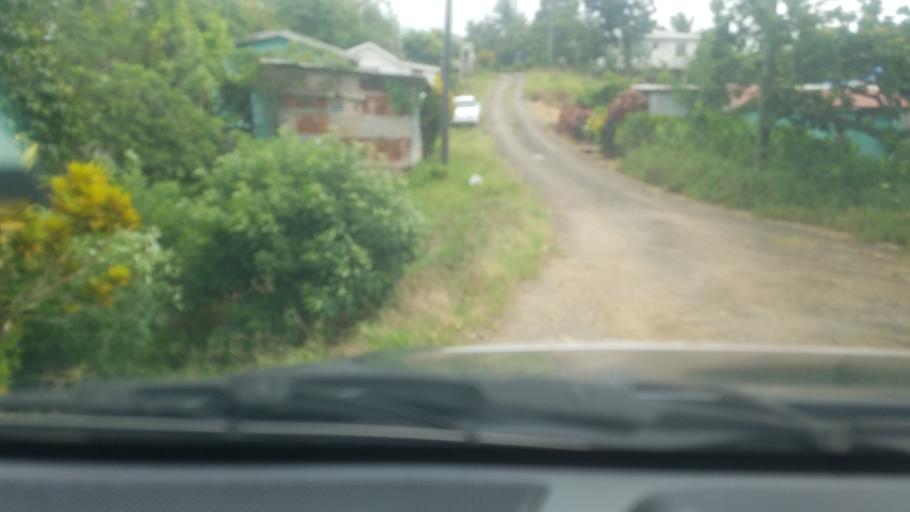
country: LC
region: Micoud Quarter
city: Micoud
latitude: 13.8043
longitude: -60.9414
